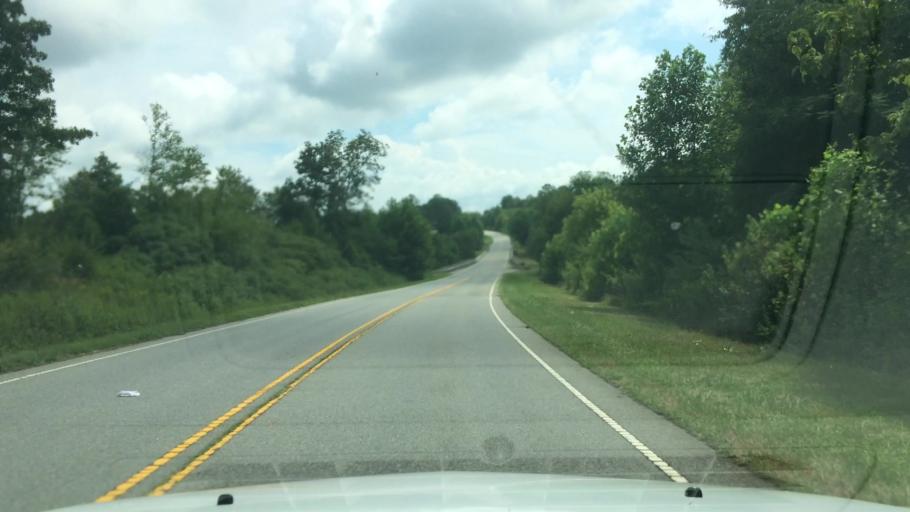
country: US
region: North Carolina
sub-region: Yadkin County
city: Jonesville
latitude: 36.1215
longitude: -80.8534
